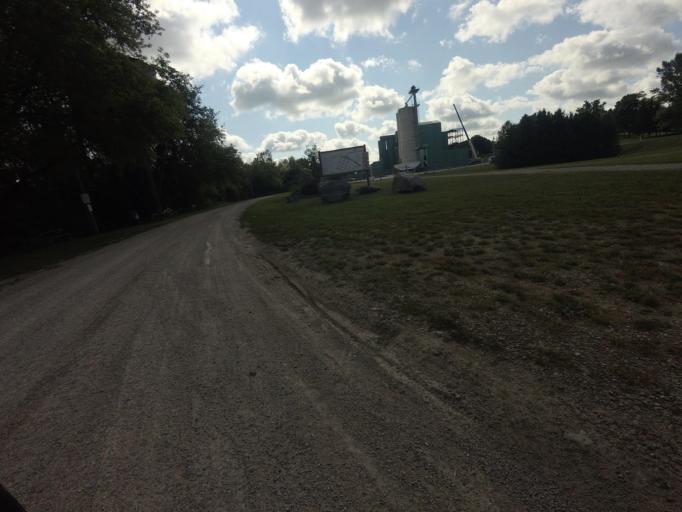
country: CA
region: Ontario
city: Huron East
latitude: 43.7387
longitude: -81.4270
